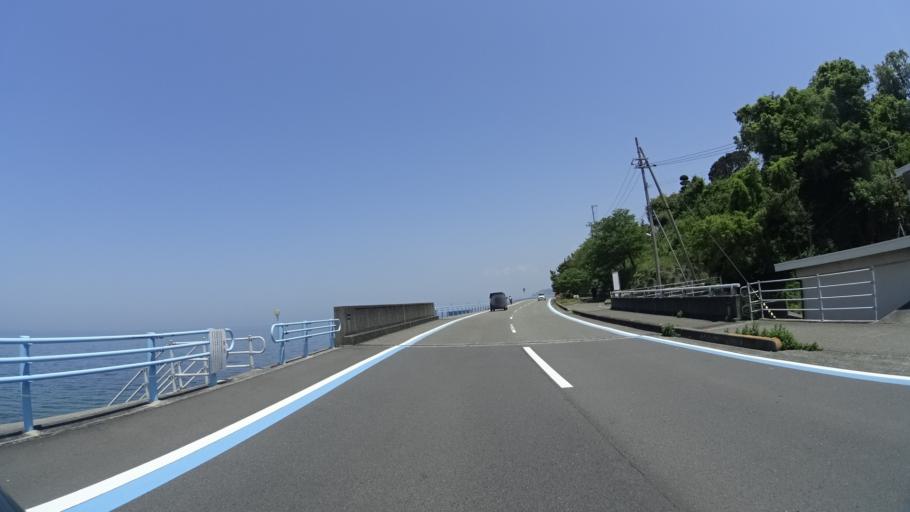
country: JP
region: Ehime
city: Iyo
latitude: 33.6826
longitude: 132.6294
